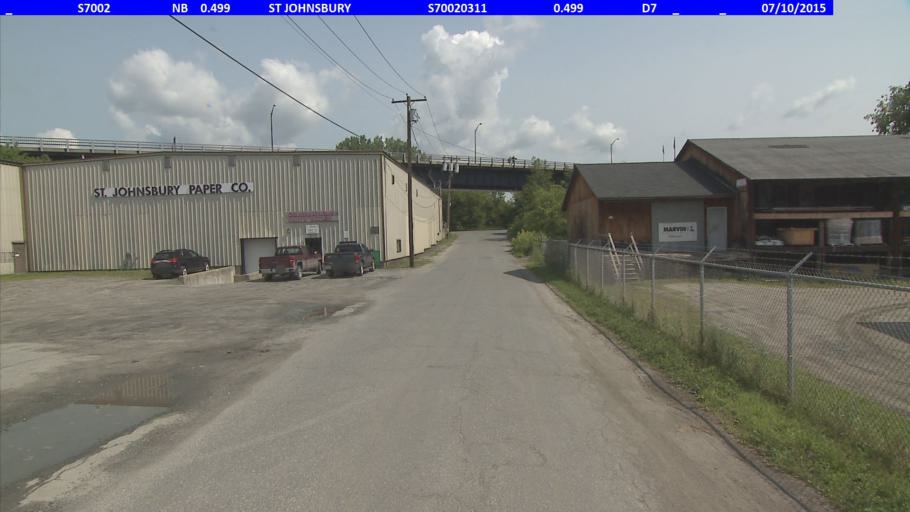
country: US
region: Vermont
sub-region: Caledonia County
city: Saint Johnsbury
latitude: 44.4188
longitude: -72.0139
